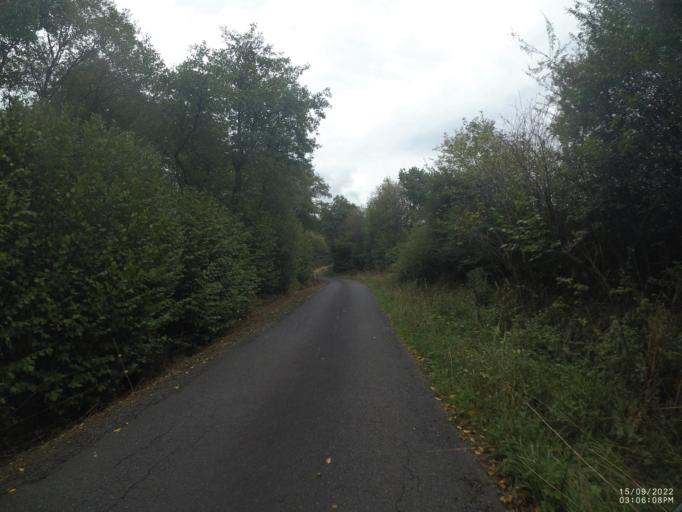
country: DE
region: Rheinland-Pfalz
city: Bongard
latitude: 50.2940
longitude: 6.8138
